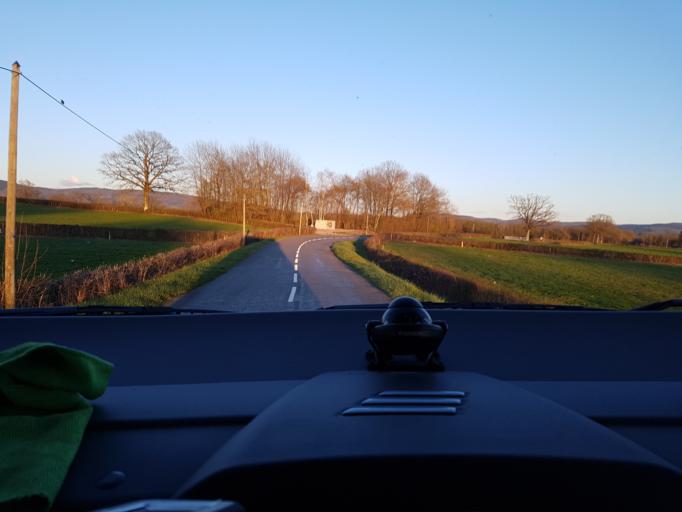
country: FR
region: Bourgogne
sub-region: Departement de Saone-et-Loire
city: Etang-sur-Arroux
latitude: 46.8879
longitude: 4.1526
